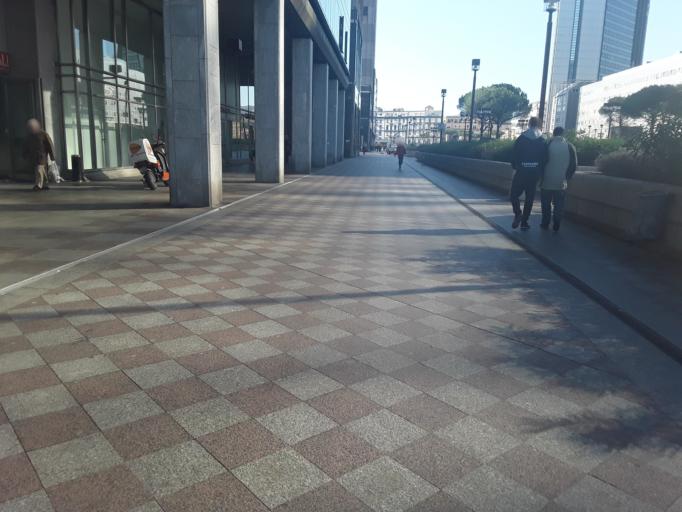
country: IT
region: Campania
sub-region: Provincia di Napoli
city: Napoli
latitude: 40.8566
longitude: 14.2806
